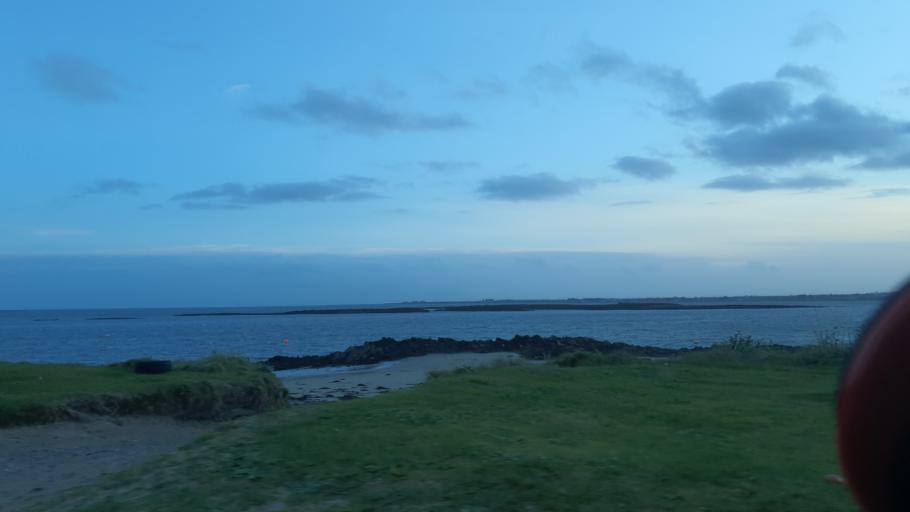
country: IE
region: Leinster
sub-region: Lu
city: Carlingford
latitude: 54.0403
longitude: -6.1055
